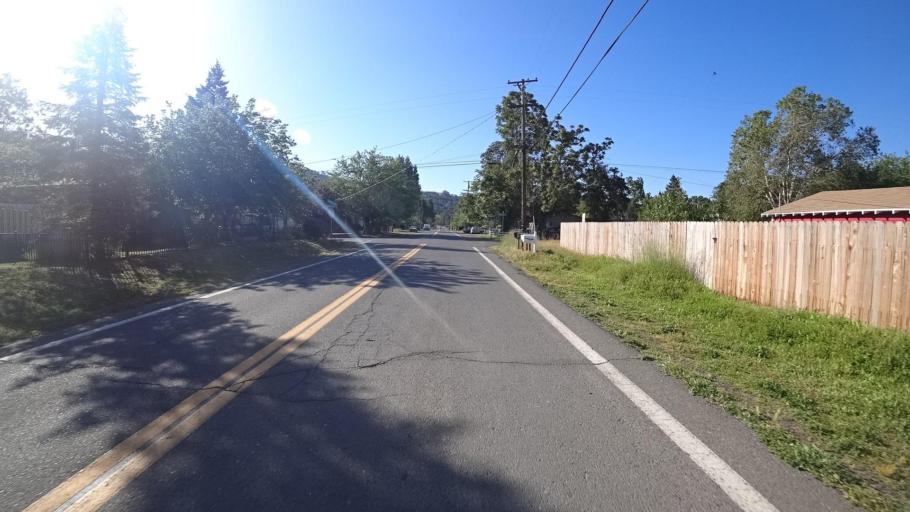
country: US
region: California
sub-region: Lake County
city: Lucerne
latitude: 39.0935
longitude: -122.7948
